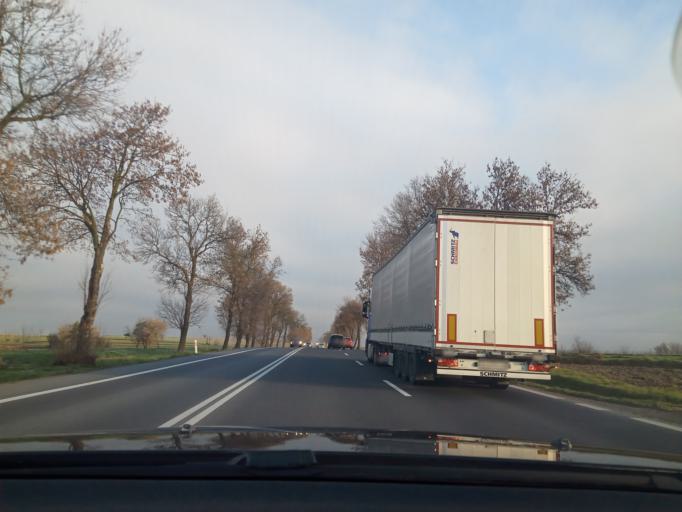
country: PL
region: Lesser Poland Voivodeship
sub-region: Powiat miechowski
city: Miechow
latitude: 50.3039
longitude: 20.0373
